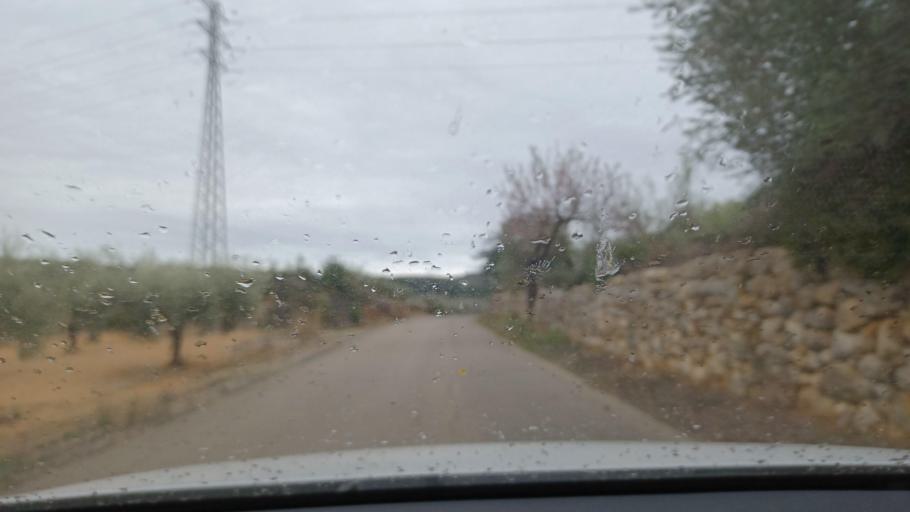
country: ES
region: Valencia
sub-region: Provincia de Castello
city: Traiguera
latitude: 40.5152
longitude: 0.2918
